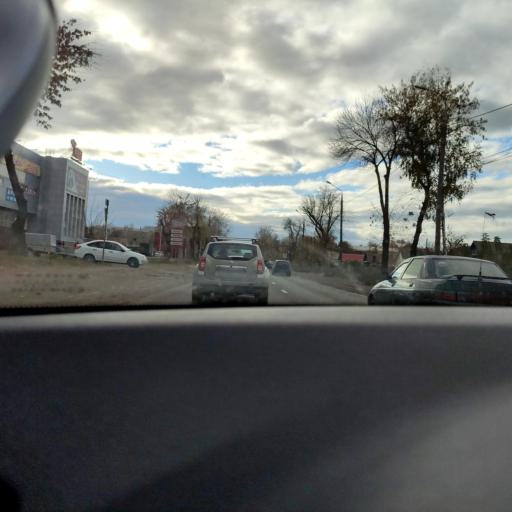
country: RU
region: Samara
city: Smyshlyayevka
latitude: 53.2303
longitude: 50.3027
